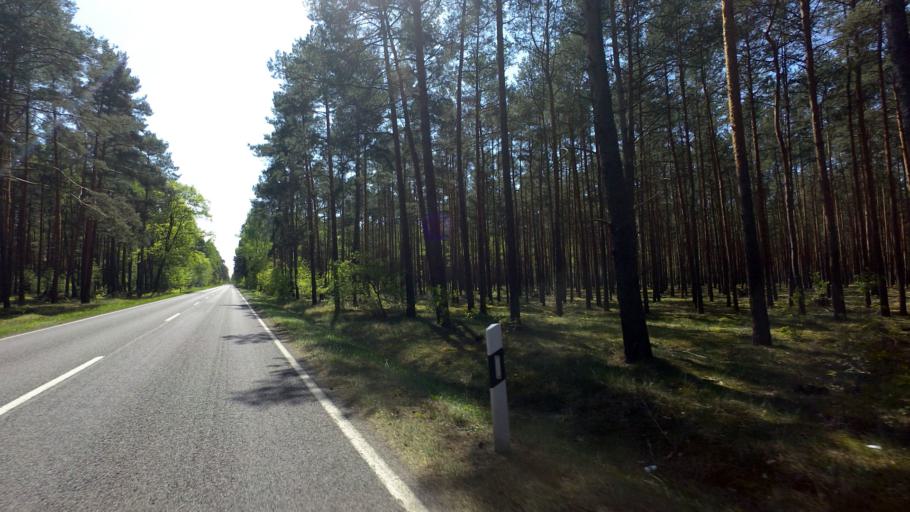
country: DE
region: Brandenburg
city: Gross Koris
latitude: 52.2055
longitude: 13.6916
